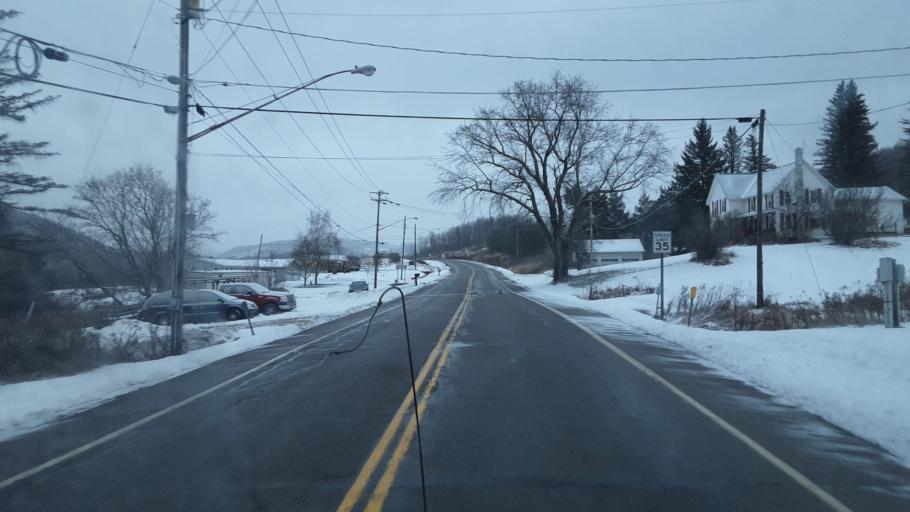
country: US
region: Pennsylvania
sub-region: Tioga County
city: Westfield
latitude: 42.0482
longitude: -77.5463
